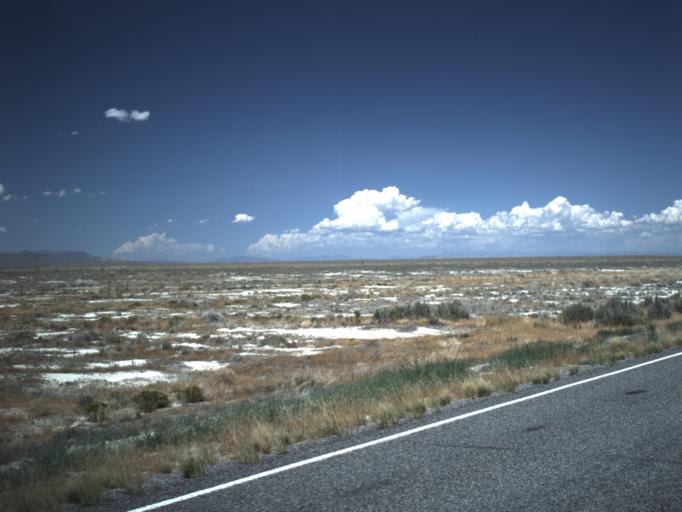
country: US
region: Utah
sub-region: Millard County
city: Delta
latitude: 39.2072
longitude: -112.9716
